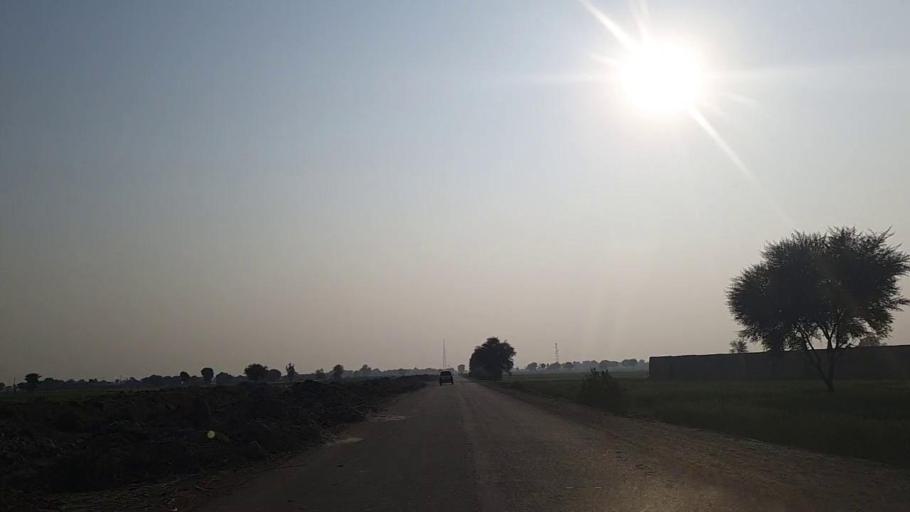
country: PK
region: Sindh
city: Shahpur Chakar
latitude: 26.2083
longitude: 68.5628
